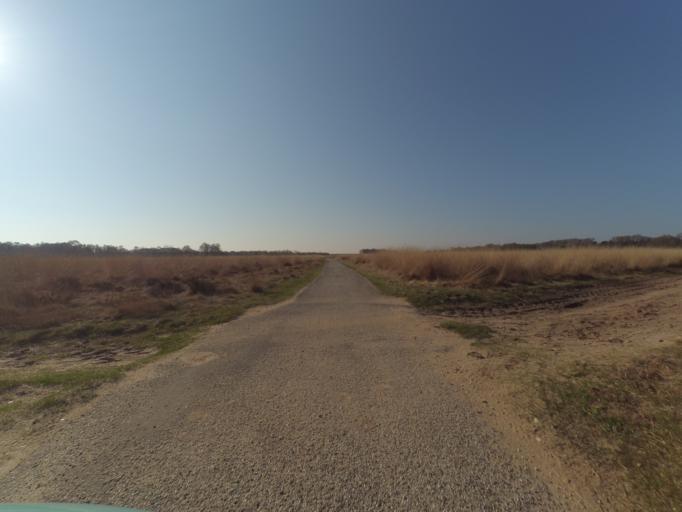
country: NL
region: Gelderland
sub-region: Gemeente Arnhem
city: Hoogkamp
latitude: 52.0665
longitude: 5.8468
